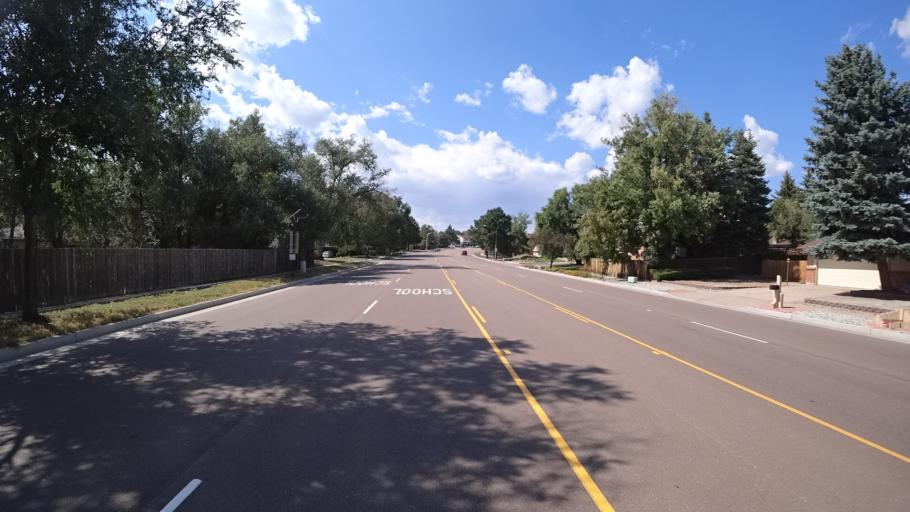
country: US
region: Colorado
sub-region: El Paso County
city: Cimarron Hills
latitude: 38.8754
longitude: -104.7515
